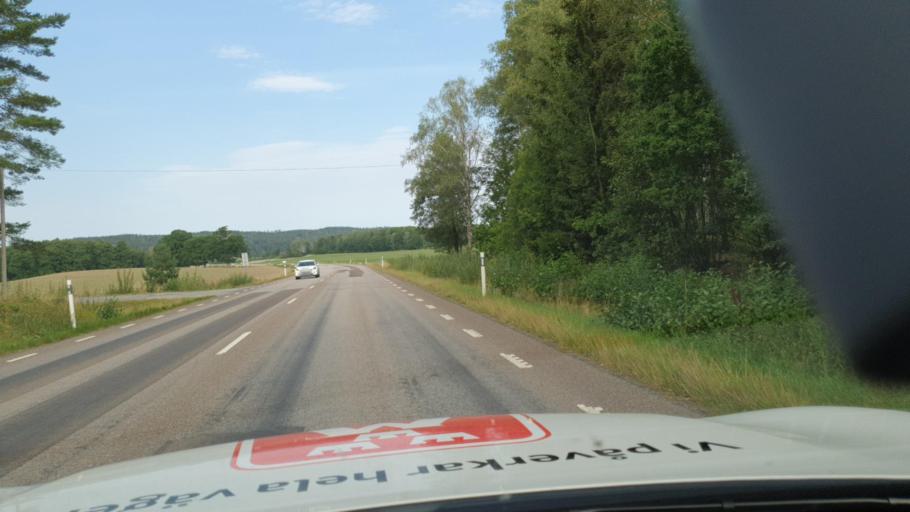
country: SE
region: Vaestra Goetaland
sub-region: Melleruds Kommun
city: Mellerud
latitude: 58.7223
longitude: 12.3969
